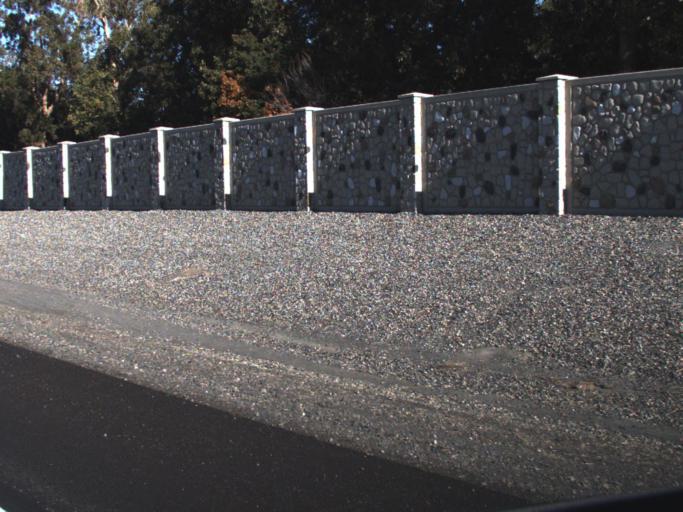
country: US
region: Washington
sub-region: Benton County
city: Richland
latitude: 46.2690
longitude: -119.3041
